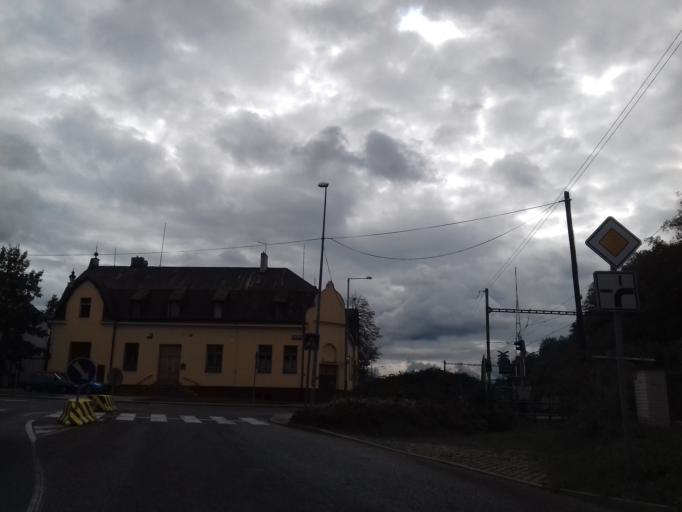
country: CZ
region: Praha
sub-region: Praha 12
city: Modrany
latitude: 50.0122
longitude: 14.3891
